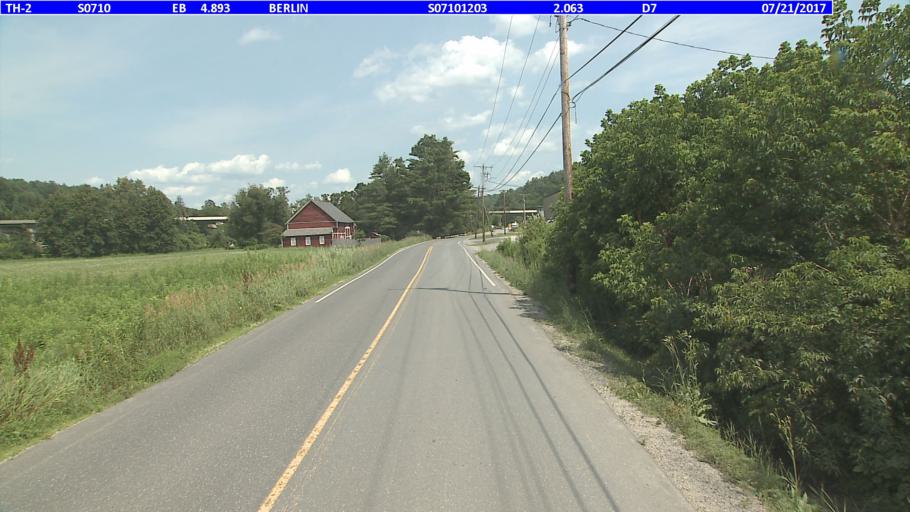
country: US
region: Vermont
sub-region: Washington County
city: Montpelier
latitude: 44.2566
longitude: -72.6044
